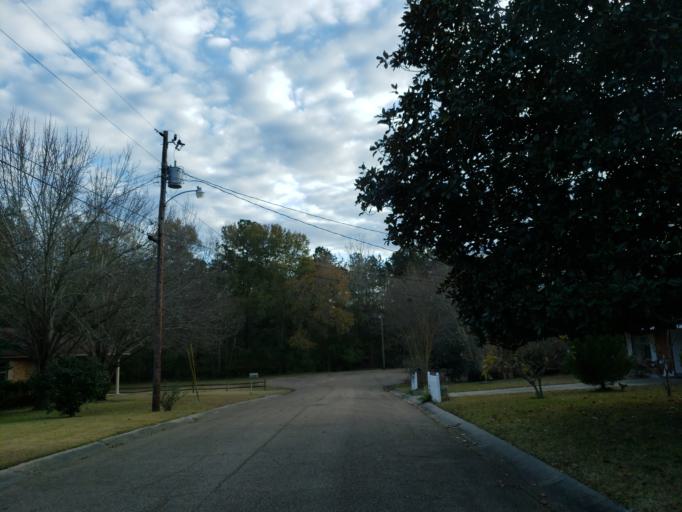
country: US
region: Mississippi
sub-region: Forrest County
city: Hattiesburg
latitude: 31.3015
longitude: -89.3295
